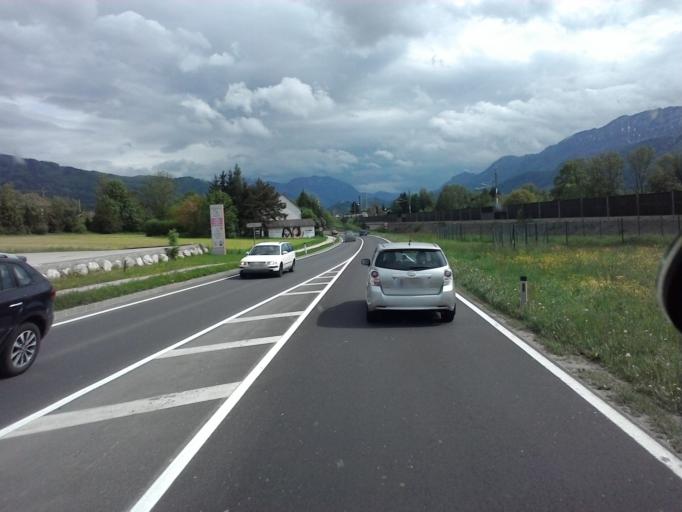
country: AT
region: Upper Austria
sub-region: Politischer Bezirk Kirchdorf an der Krems
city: Micheldorf in Oberoesterreich
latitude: 47.9155
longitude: 14.1105
